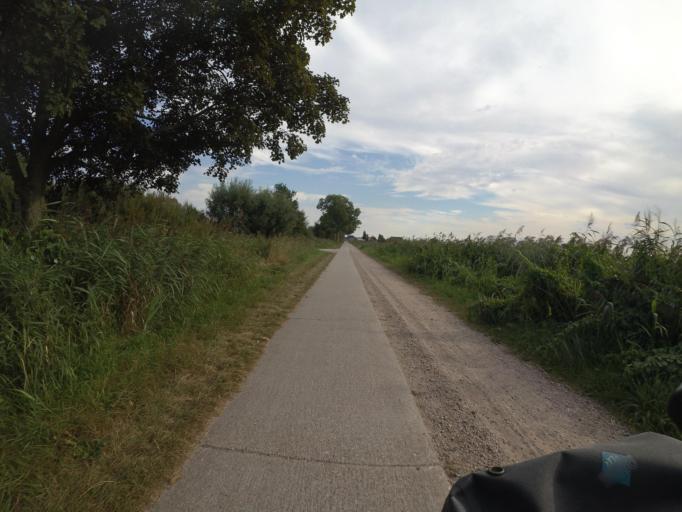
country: NL
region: Overijssel
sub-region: Gemeente Zwartewaterland
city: Hasselt
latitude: 52.6072
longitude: 6.1064
